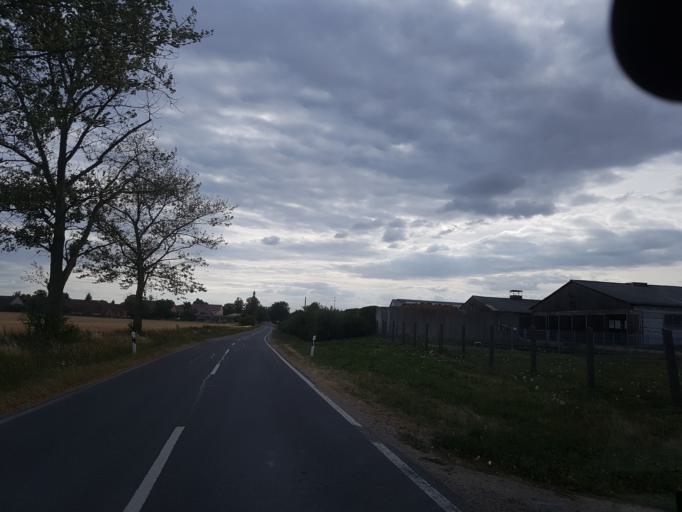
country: DE
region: Brandenburg
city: Juterbog
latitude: 51.9048
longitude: 13.1467
